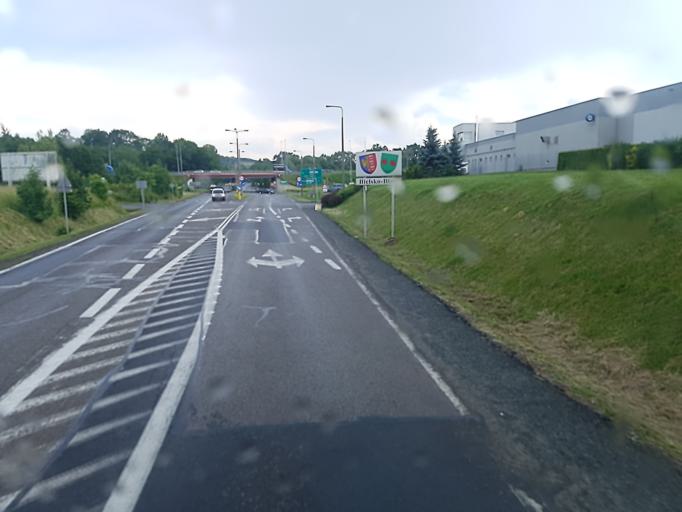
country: PL
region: Silesian Voivodeship
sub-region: Powiat bielski
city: Mazancowice
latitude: 49.8419
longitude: 18.9994
